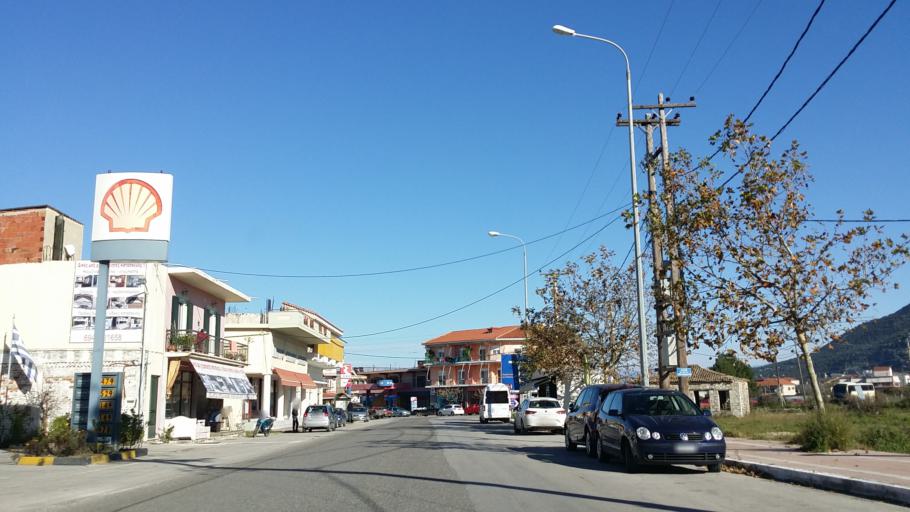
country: GR
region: West Greece
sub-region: Nomos Aitolias kai Akarnanias
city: Vonitsa
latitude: 38.9133
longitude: 20.8897
